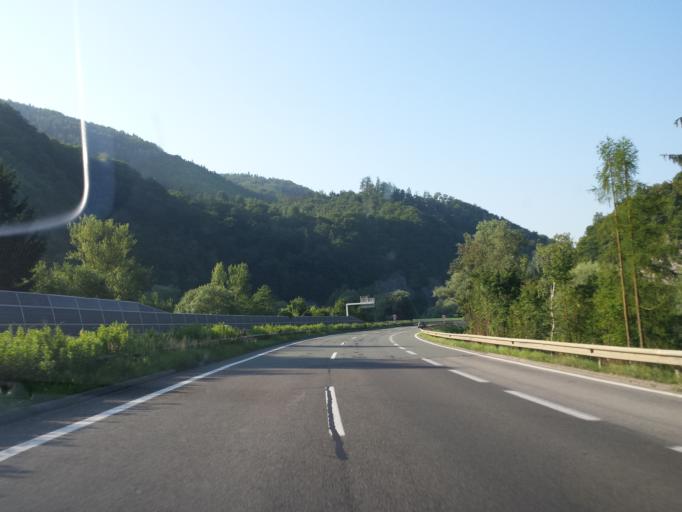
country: AT
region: Styria
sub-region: Politischer Bezirk Graz-Umgebung
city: Peggau
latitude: 47.2283
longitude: 15.3410
